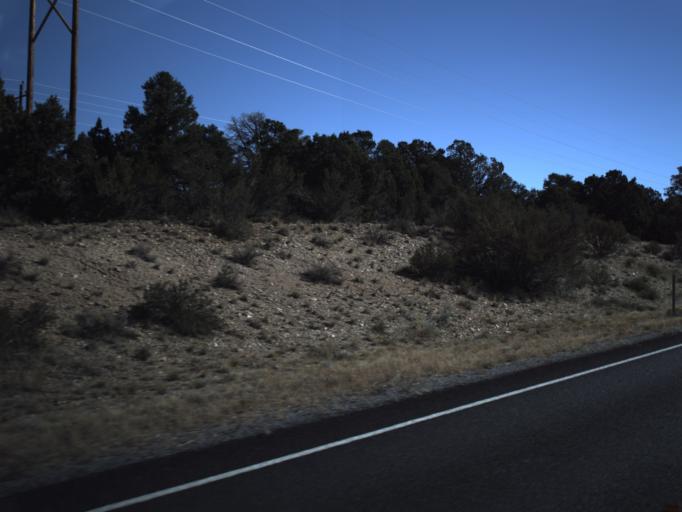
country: US
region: Utah
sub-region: Washington County
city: Enterprise
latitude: 37.6112
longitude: -113.3886
